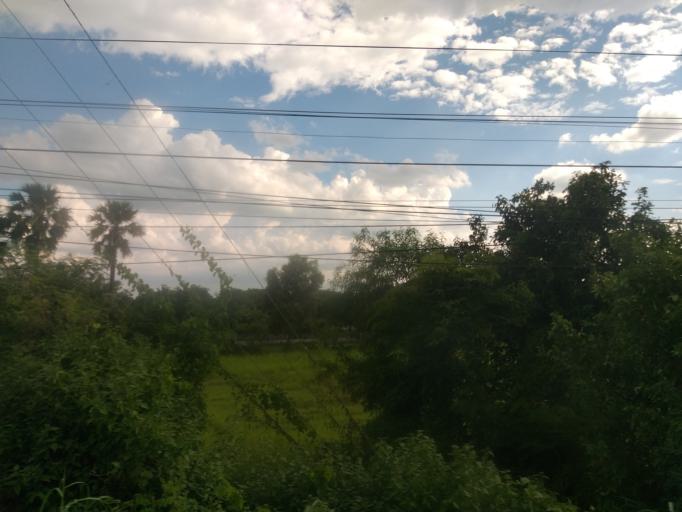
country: TH
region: Nakhon Nayok
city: Nakhon Nayok
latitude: 14.2137
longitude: 101.1725
